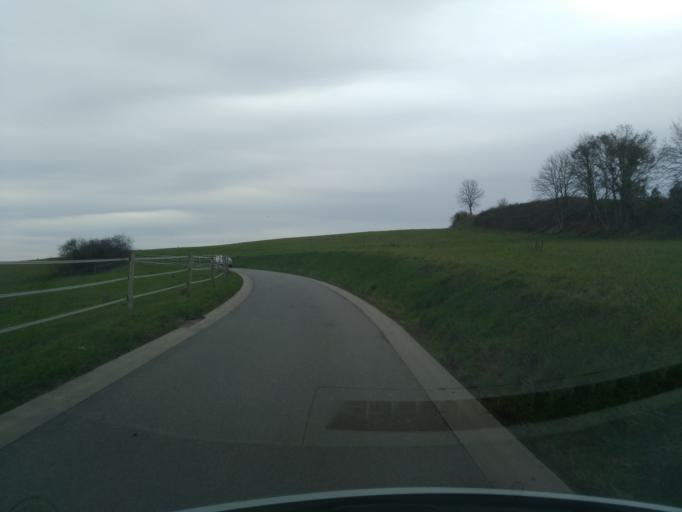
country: FR
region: Ile-de-France
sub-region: Departement des Yvelines
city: Chavenay
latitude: 48.8489
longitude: 1.9867
